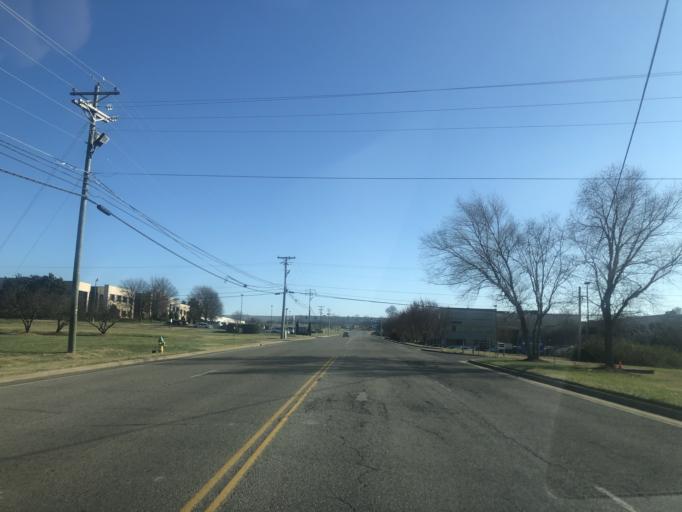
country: US
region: Tennessee
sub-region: Rutherford County
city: La Vergne
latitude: 35.9991
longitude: -86.5912
